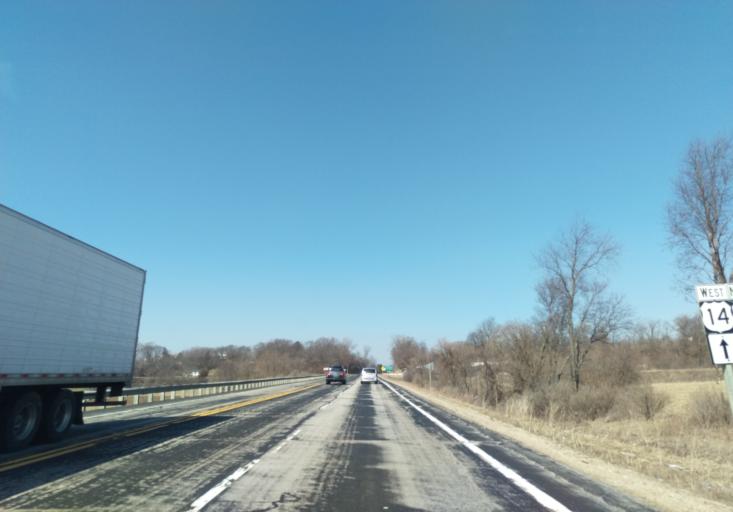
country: US
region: Wisconsin
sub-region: Vernon County
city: Viroqua
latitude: 43.5197
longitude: -90.8625
